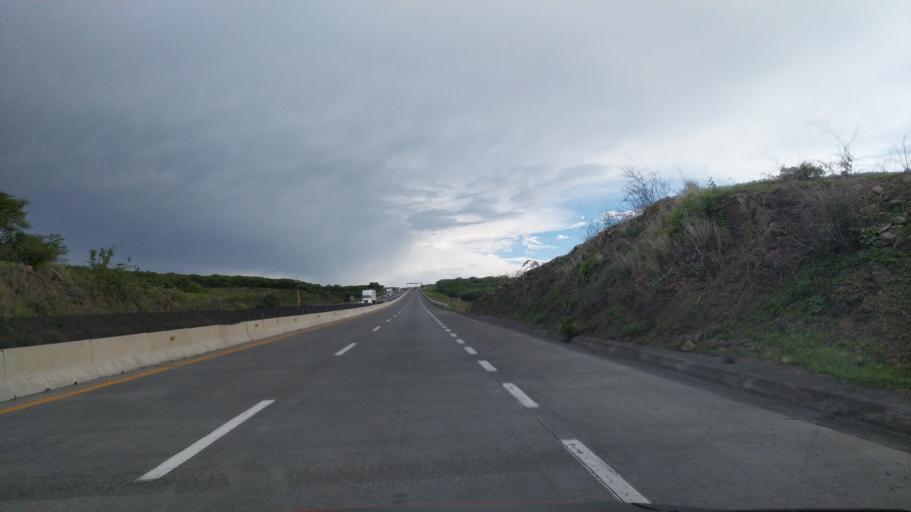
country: MX
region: Jalisco
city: Degollado
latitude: 20.3775
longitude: -102.1229
